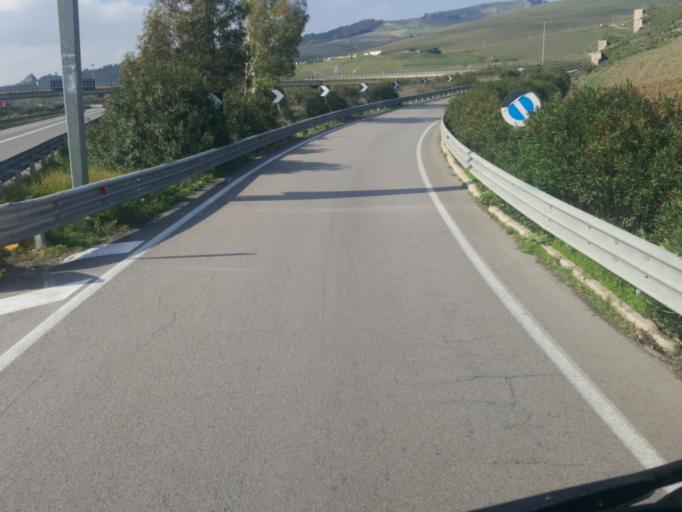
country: IT
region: Sicily
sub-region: Enna
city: Pietraperzia
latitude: 37.4581
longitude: 14.1110
